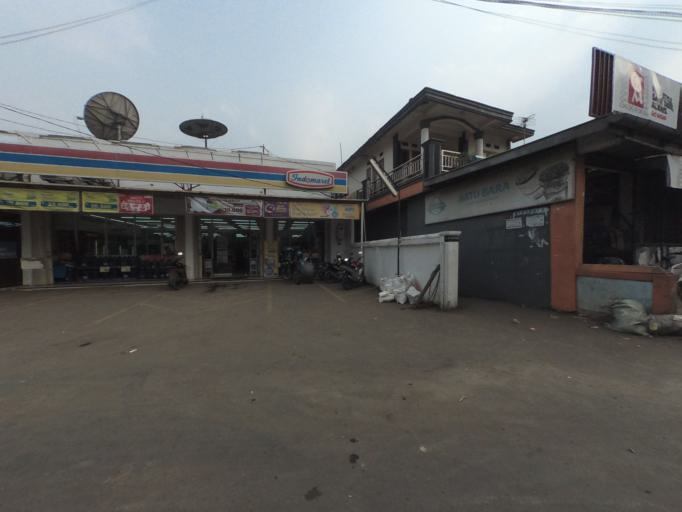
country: ID
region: West Java
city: Ciampea
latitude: -6.5594
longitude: 106.6909
